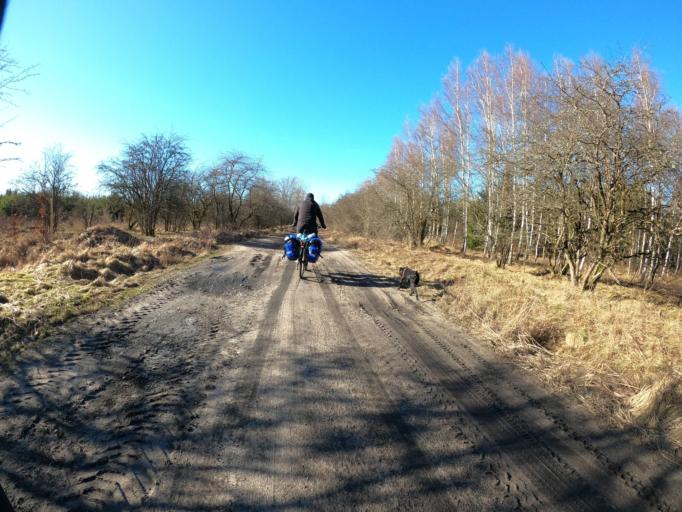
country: PL
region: West Pomeranian Voivodeship
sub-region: Powiat szczecinecki
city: Borne Sulinowo
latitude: 53.5478
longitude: 16.5590
